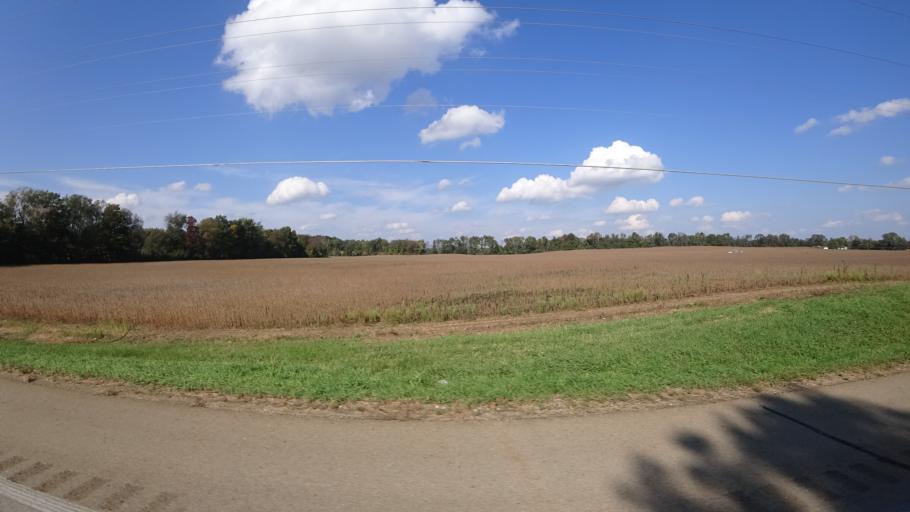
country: US
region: Michigan
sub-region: Jackson County
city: Concord
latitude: 42.1636
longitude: -84.6995
